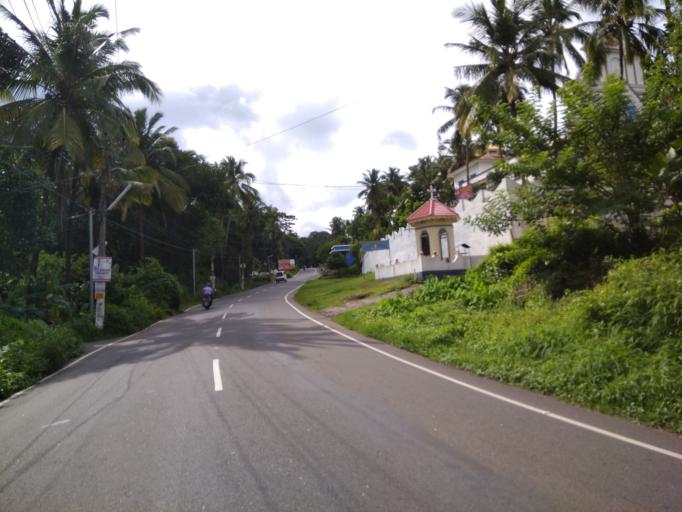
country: IN
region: Kerala
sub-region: Thrissur District
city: Trichur
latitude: 10.5352
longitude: 76.3376
